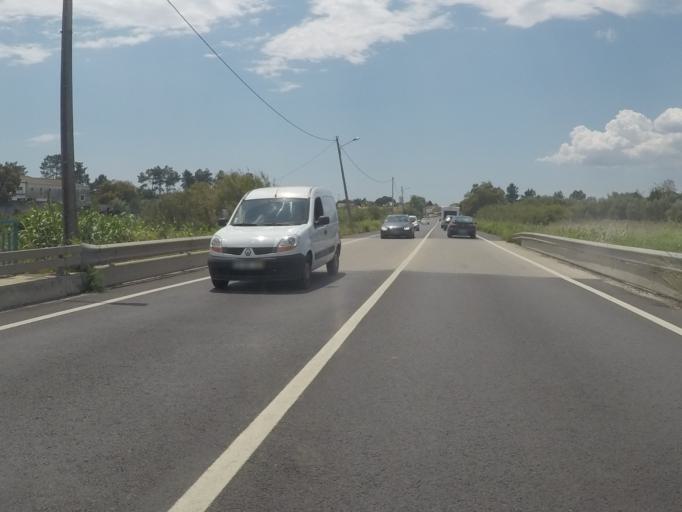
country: PT
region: Setubal
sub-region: Setubal
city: Setubal
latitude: 38.5488
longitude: -8.8129
